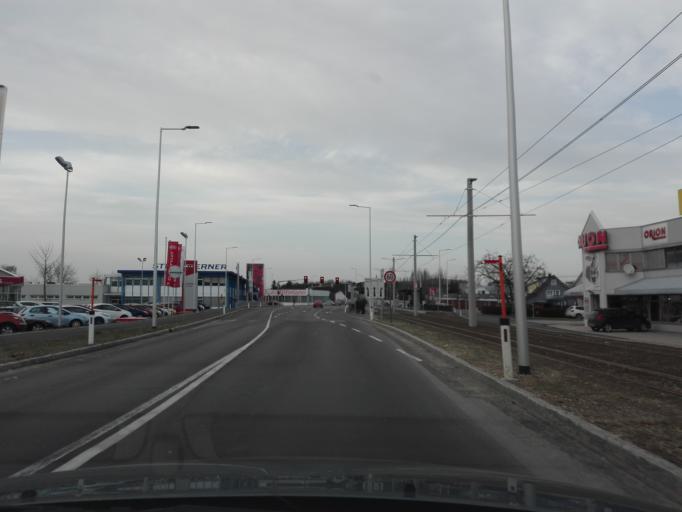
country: AT
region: Upper Austria
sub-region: Politischer Bezirk Linz-Land
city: Traun
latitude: 48.2367
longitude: 14.2355
